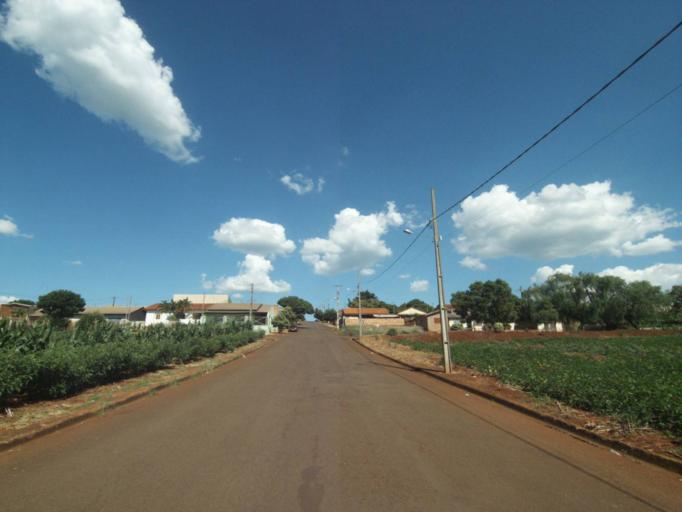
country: BR
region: Parana
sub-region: Sertanopolis
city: Sertanopolis
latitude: -23.0373
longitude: -50.8137
